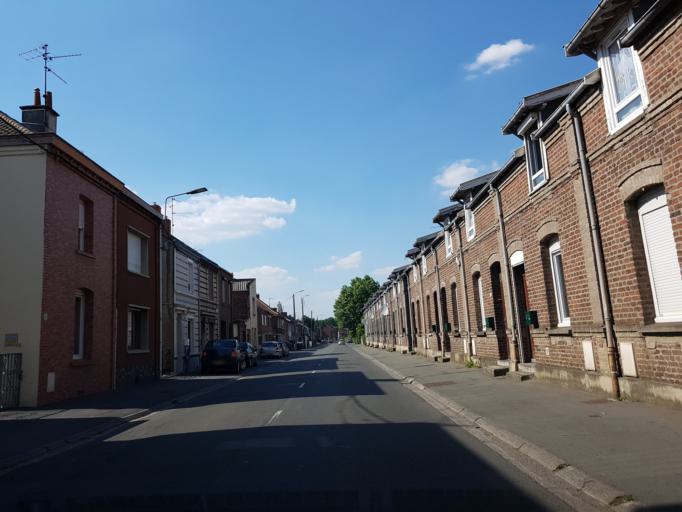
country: FR
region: Nord-Pas-de-Calais
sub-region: Departement du Nord
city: Lourches
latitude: 50.3141
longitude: 3.3438
